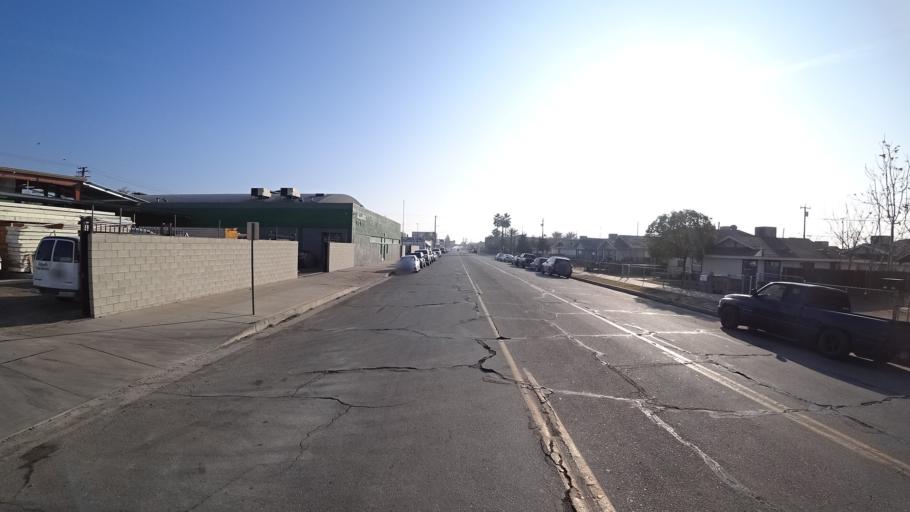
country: US
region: California
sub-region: Kern County
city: Bakersfield
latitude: 35.3795
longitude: -118.9948
